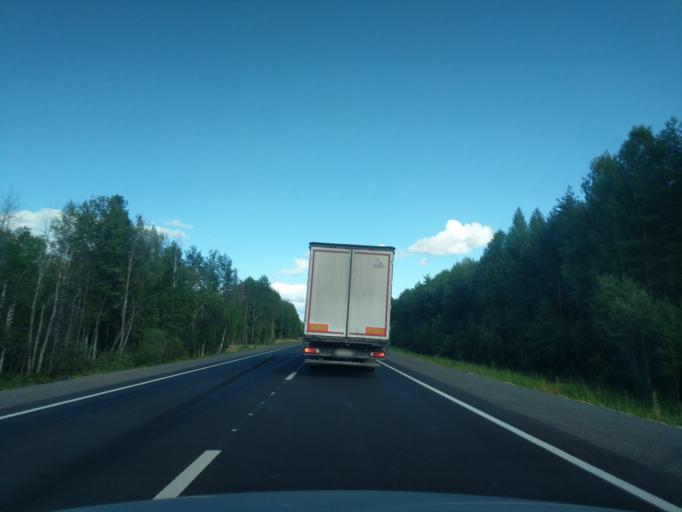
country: RU
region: Kostroma
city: Makar'yev
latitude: 57.8481
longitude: 43.6715
